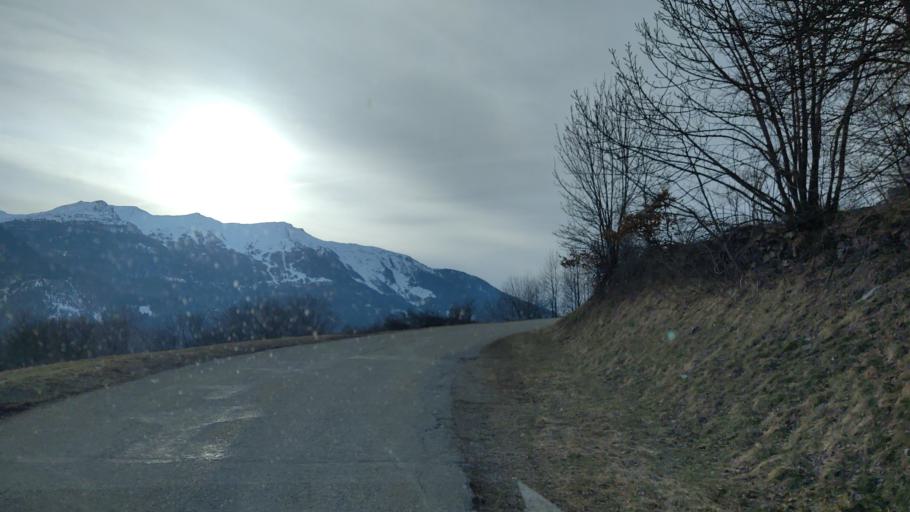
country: FR
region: Rhone-Alpes
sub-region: Departement de la Savoie
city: Saint-Michel-de-Maurienne
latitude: 45.2439
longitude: 6.4644
